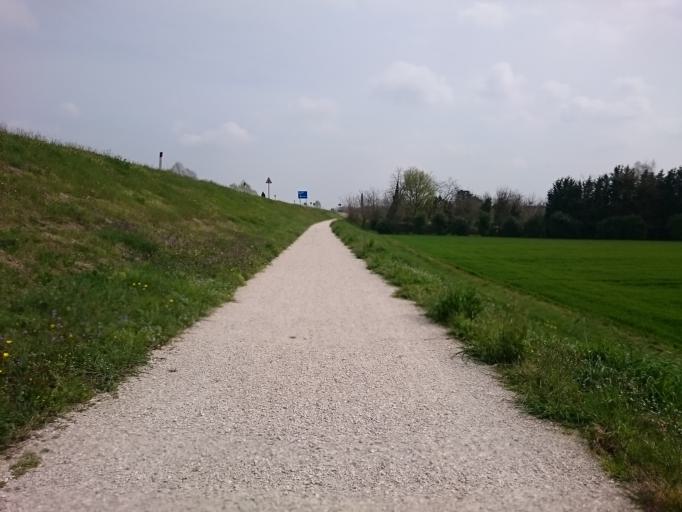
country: IT
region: Veneto
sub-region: Provincia di Padova
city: Pontelongo
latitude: 45.2518
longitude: 12.0089
